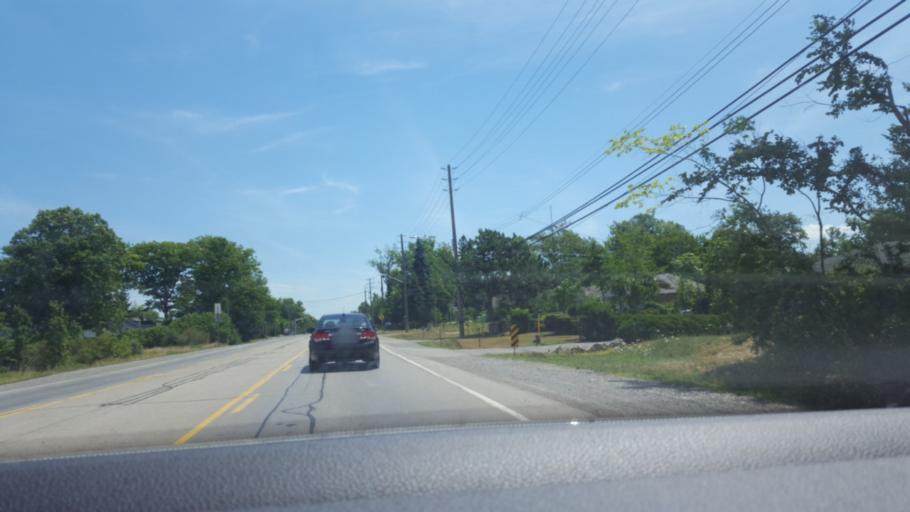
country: CA
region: Ontario
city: Hamilton
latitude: 43.1957
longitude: -79.8625
